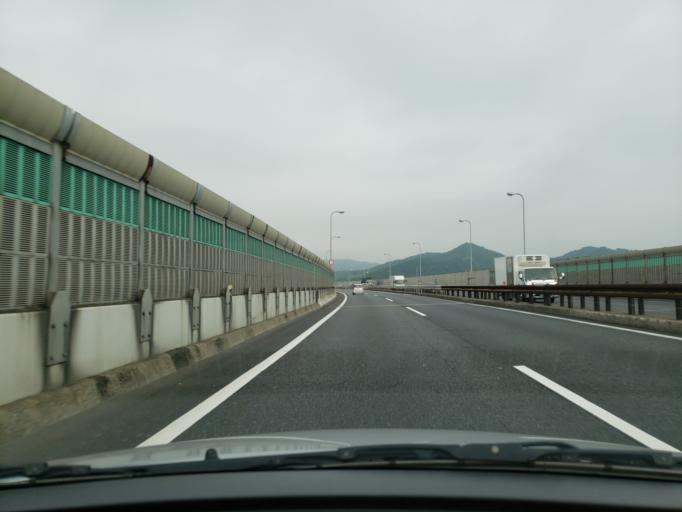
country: JP
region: Hyogo
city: Himeji
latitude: 34.8166
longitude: 134.6676
